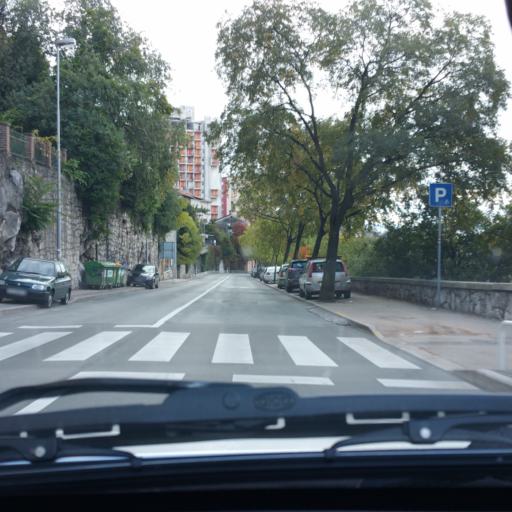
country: HR
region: Primorsko-Goranska
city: Drenova
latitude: 45.3364
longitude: 14.4328
